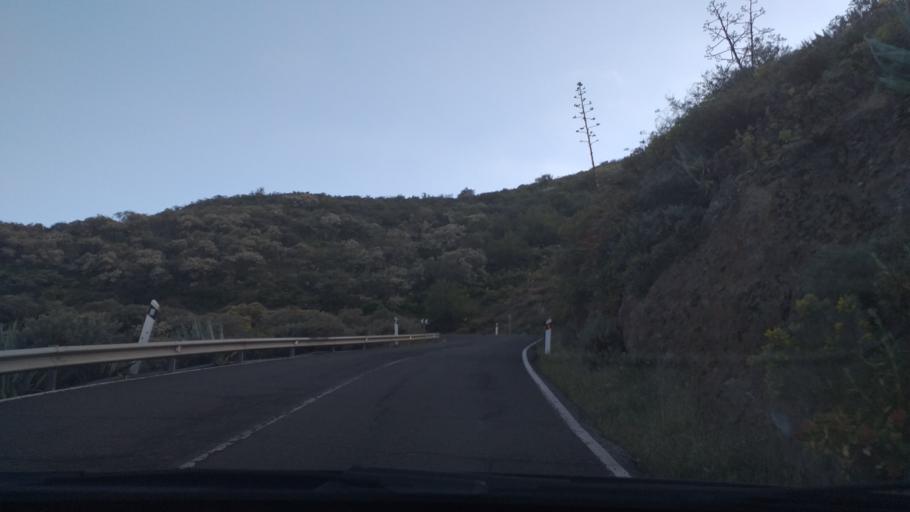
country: ES
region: Canary Islands
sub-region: Provincia de Las Palmas
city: Valsequillo de Gran Canaria
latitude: 27.9587
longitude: -15.4934
